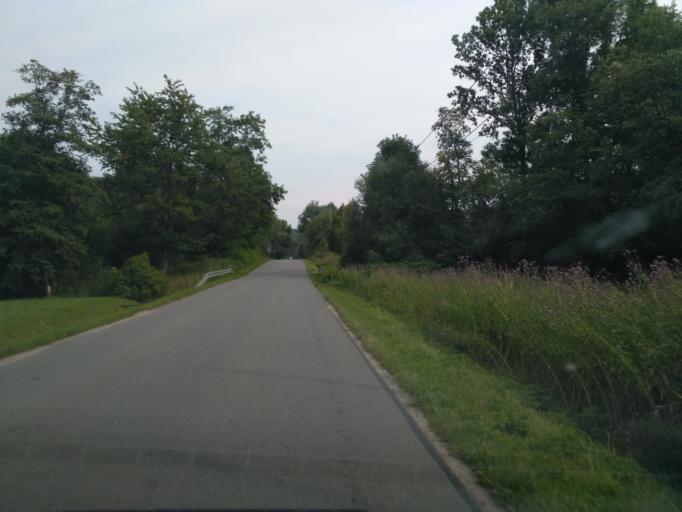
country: PL
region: Subcarpathian Voivodeship
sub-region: Powiat strzyzowski
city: Gwoznica Gorna
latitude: 49.8394
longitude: 21.9841
